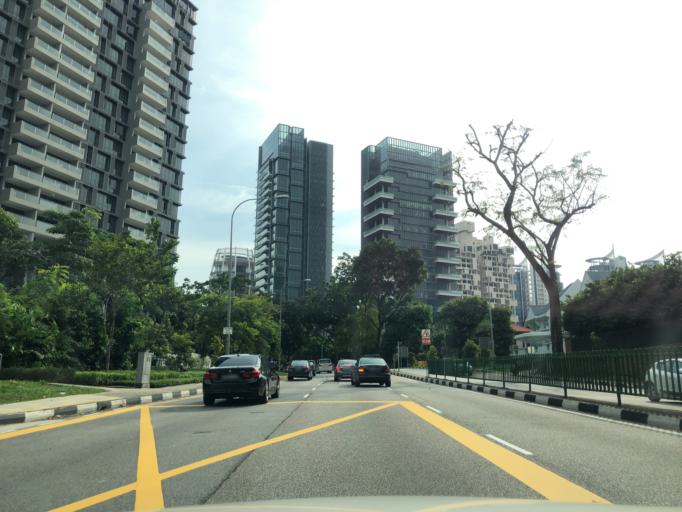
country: SG
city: Singapore
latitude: 1.3022
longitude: 103.8299
